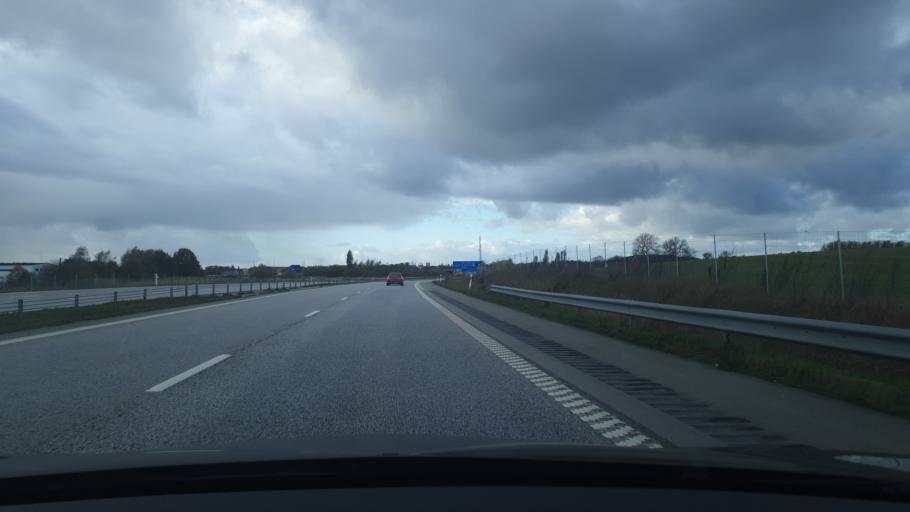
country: SE
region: Skane
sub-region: Svedala Kommun
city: Svedala
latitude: 55.5147
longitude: 13.2589
